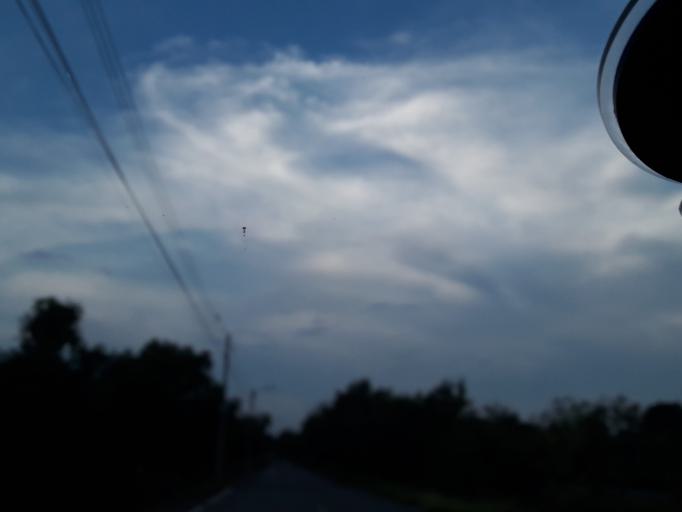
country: TH
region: Pathum Thani
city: Nong Suea
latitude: 14.2070
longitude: 100.8689
